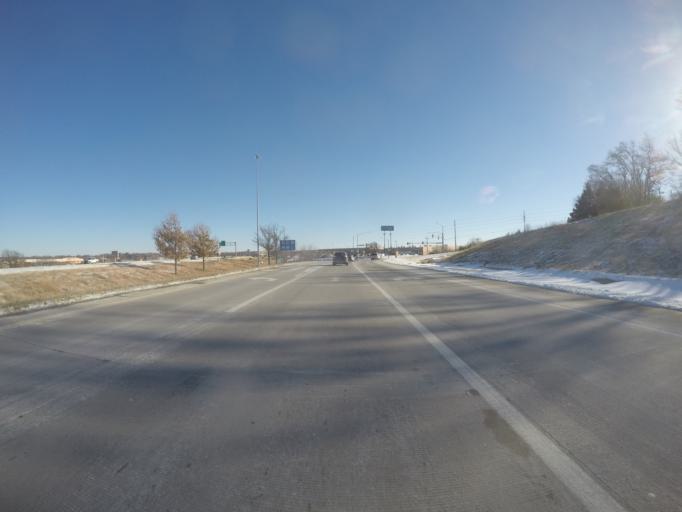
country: US
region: Kansas
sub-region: Shawnee County
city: Topeka
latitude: 39.0445
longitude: -95.7667
